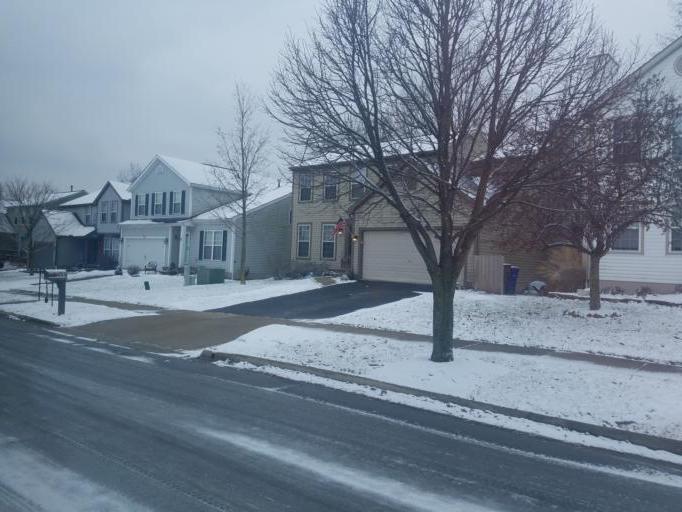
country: US
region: Ohio
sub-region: Franklin County
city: Reynoldsburg
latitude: 39.9976
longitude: -82.7863
